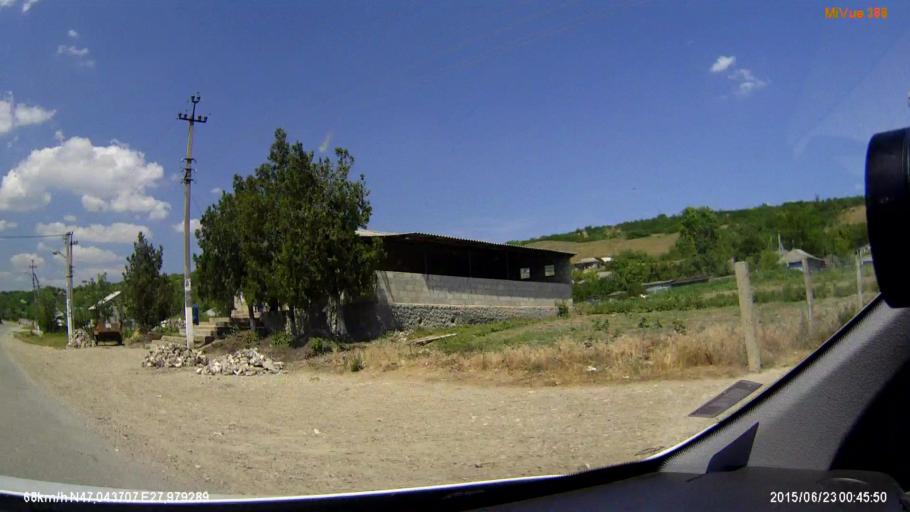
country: RO
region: Iasi
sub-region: Comuna Grozesti
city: Grozesti
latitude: 47.0436
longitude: 27.9794
